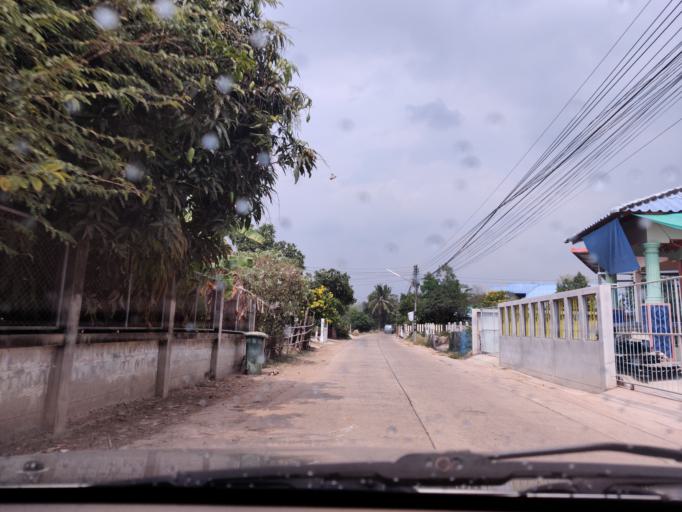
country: TH
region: Sisaket
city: Si Sa Ket
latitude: 15.1049
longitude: 104.3543
